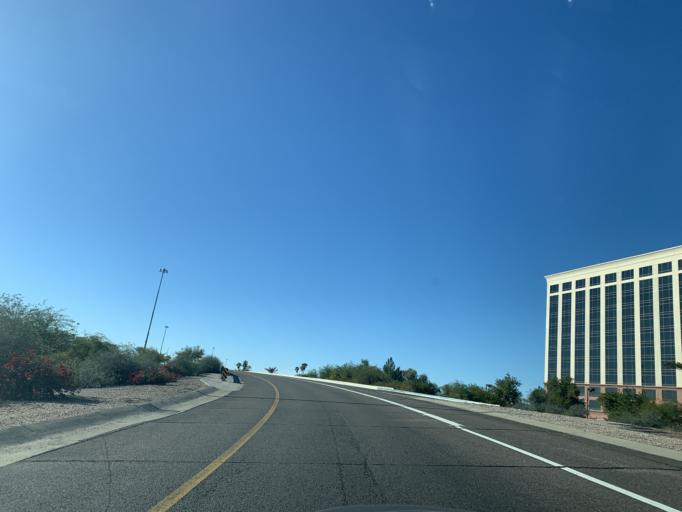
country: US
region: Arizona
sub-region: Maricopa County
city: Tempe Junction
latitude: 33.4593
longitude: -111.9850
